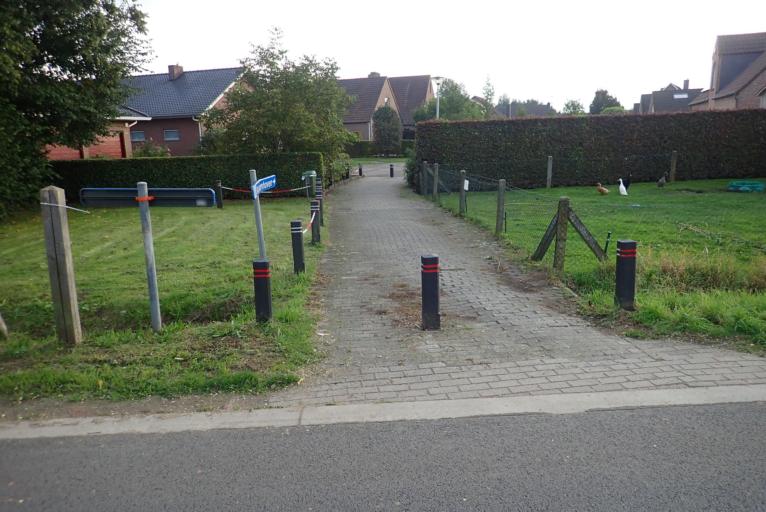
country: BE
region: Flanders
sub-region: Provincie Antwerpen
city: Zandhoven
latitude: 51.2030
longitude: 4.6444
